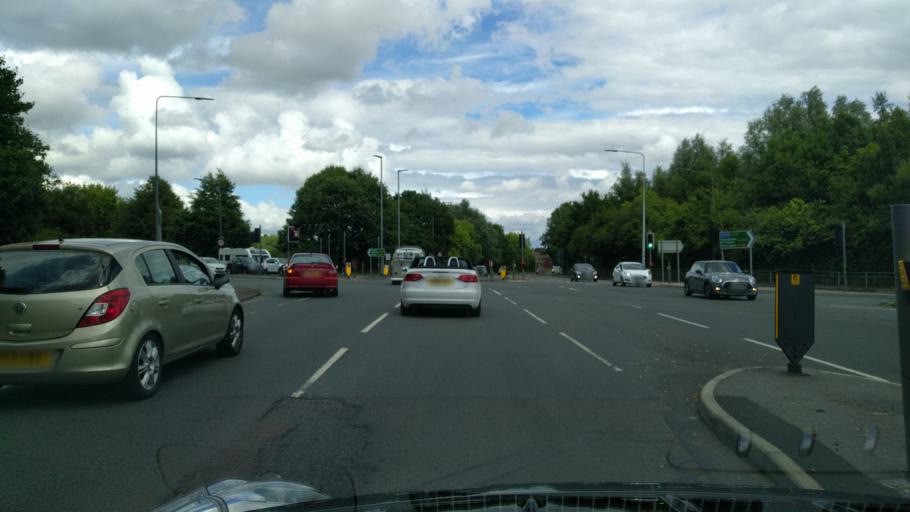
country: GB
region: England
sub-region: Borough of Wigan
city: Leigh
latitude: 53.4831
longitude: -2.5349
